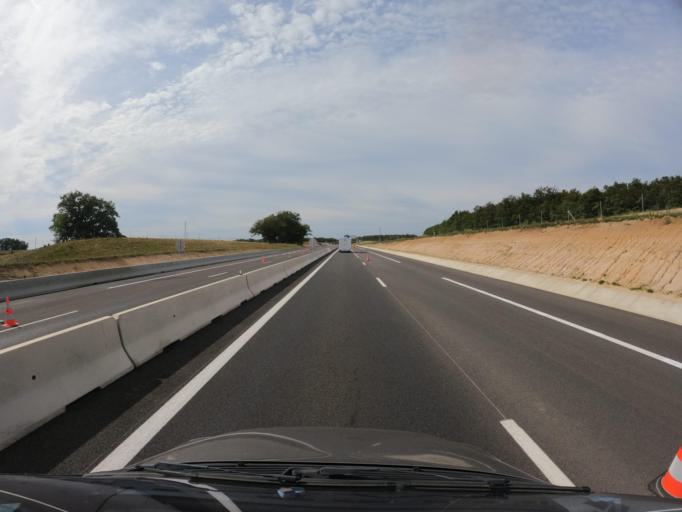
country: FR
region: Auvergne
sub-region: Departement de l'Allier
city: Neuilly-le-Real
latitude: 46.5154
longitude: 3.4657
